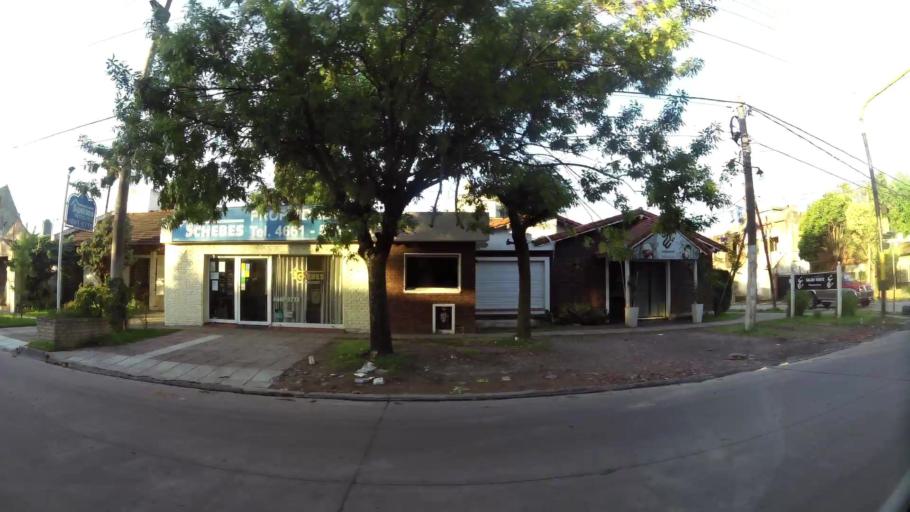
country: AR
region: Buenos Aires
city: Ituzaingo
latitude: -34.6446
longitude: -58.6469
